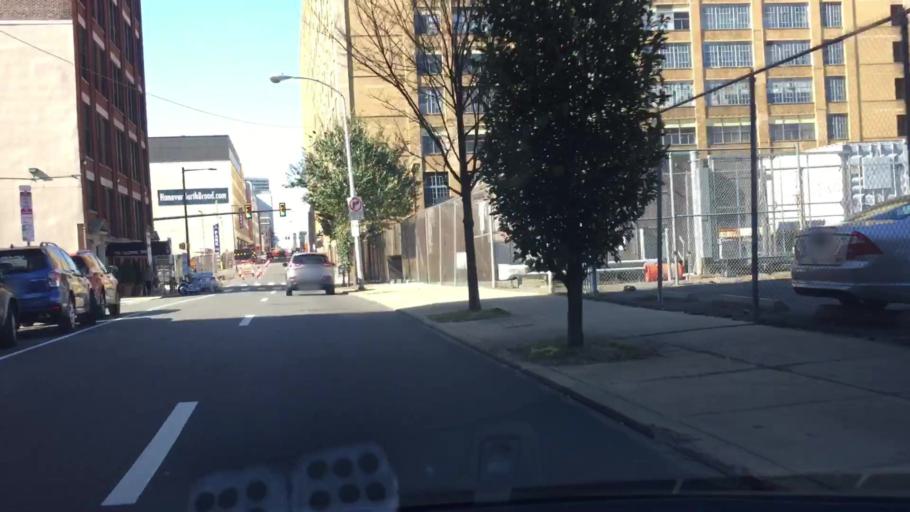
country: US
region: Pennsylvania
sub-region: Philadelphia County
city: Philadelphia
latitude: 39.9593
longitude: -75.1589
